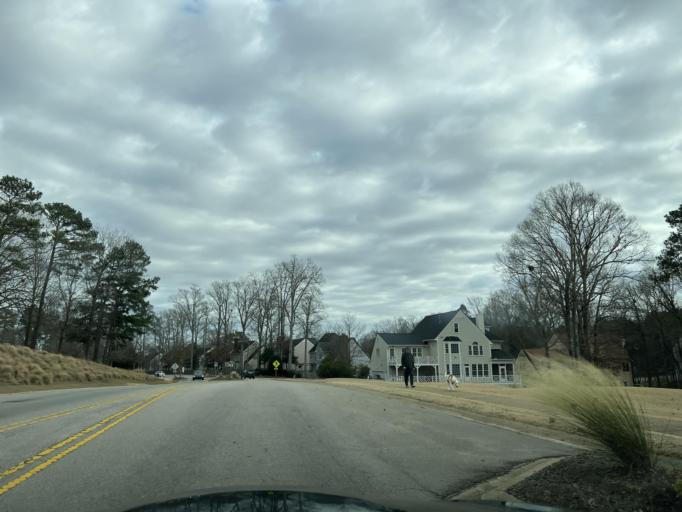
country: US
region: North Carolina
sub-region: Wake County
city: Knightdale
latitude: 35.8099
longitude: -78.5539
